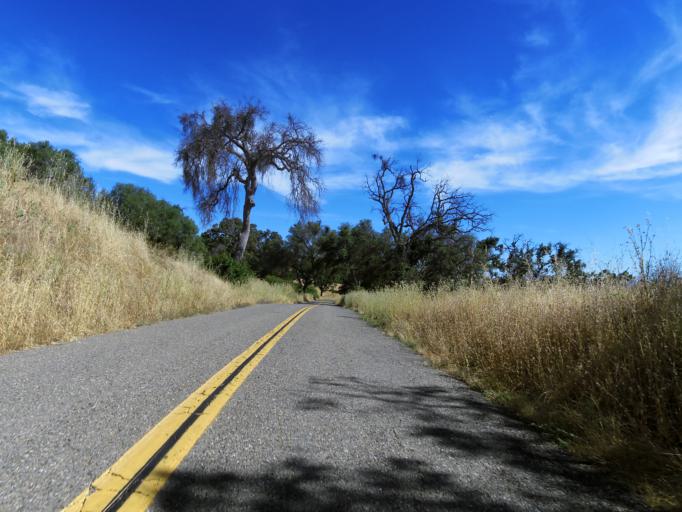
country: US
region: California
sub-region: Mariposa County
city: Mariposa
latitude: 37.3870
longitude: -119.9695
